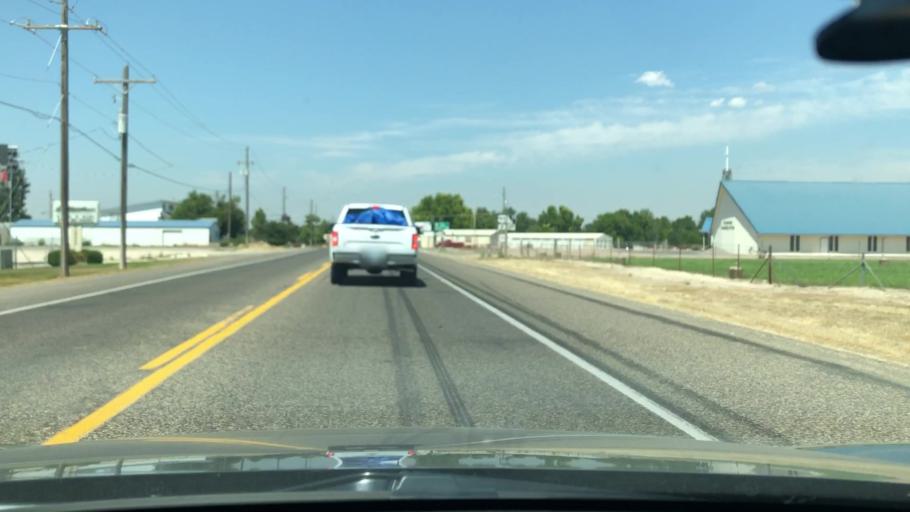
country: US
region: Idaho
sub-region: Canyon County
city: Wilder
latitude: 43.6666
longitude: -116.9117
